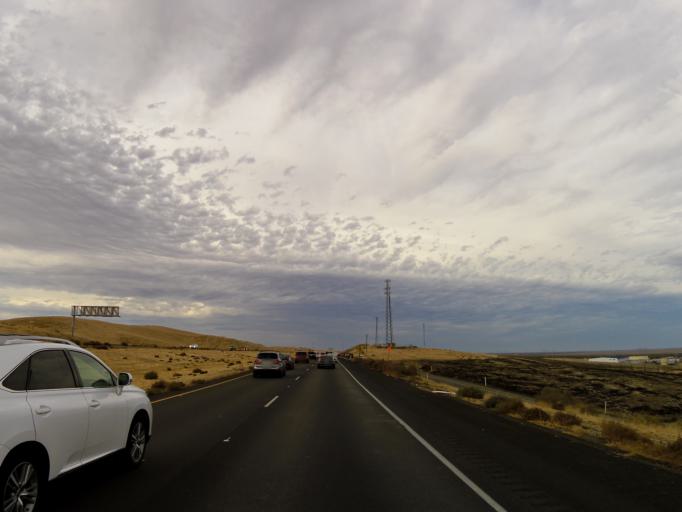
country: US
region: California
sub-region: Kings County
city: Kettleman City
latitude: 35.9839
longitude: -119.9623
